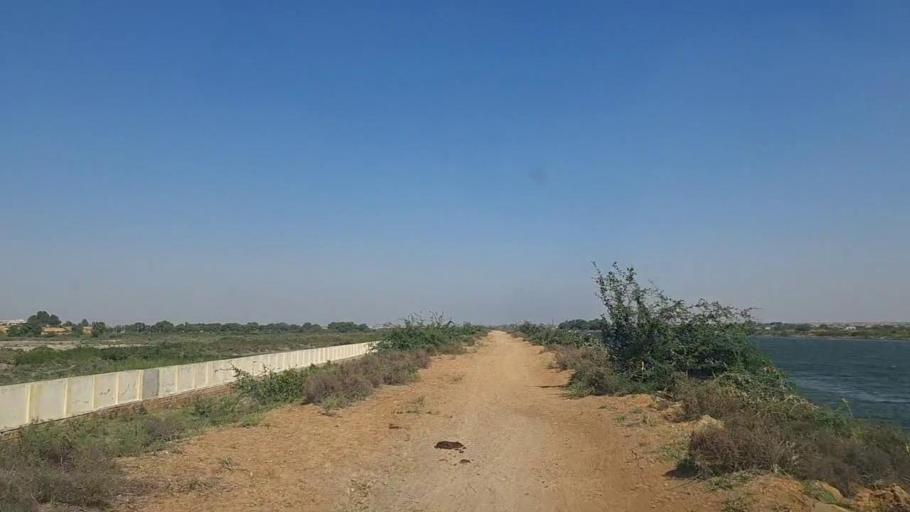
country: PK
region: Sindh
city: Thatta
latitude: 24.8135
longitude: 67.9875
